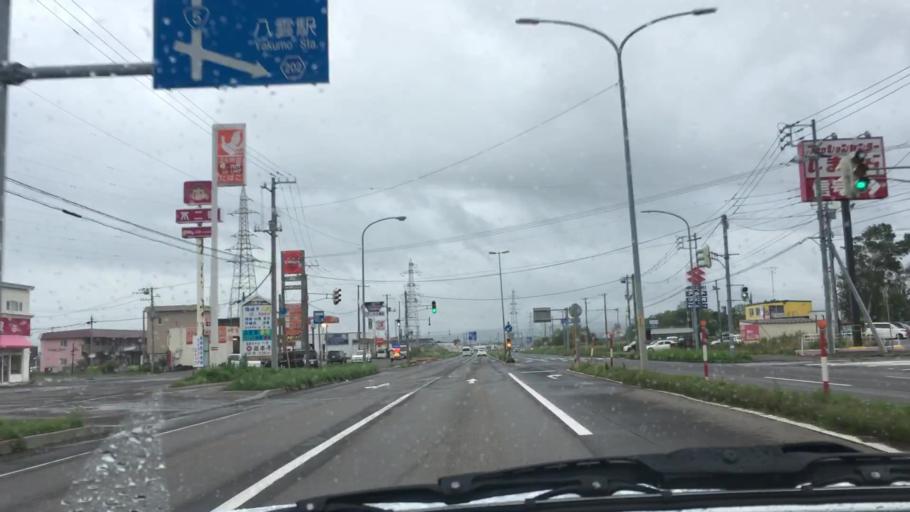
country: JP
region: Hokkaido
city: Nanae
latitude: 42.2569
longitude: 140.2799
